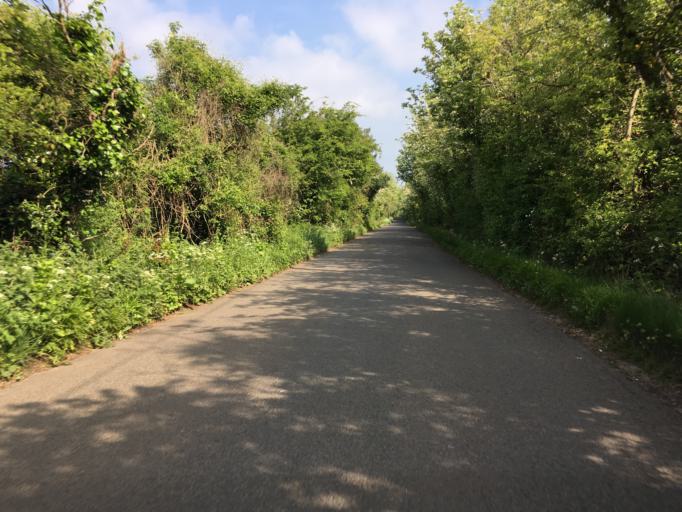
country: GB
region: England
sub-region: North Somerset
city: Nailsea
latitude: 51.4050
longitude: -2.7166
